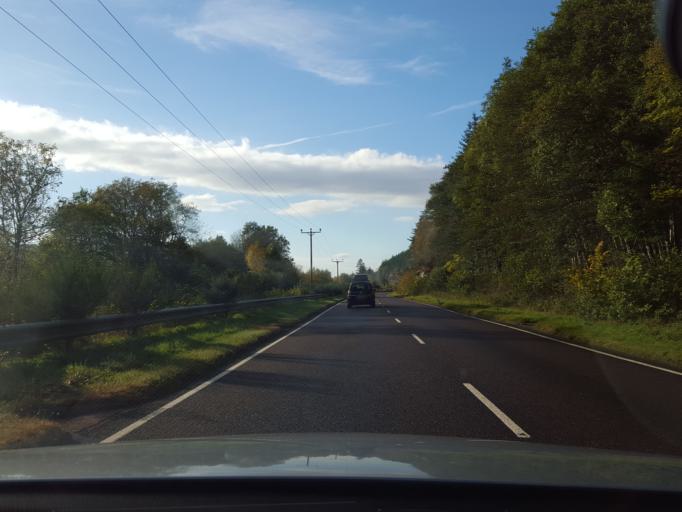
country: GB
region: Scotland
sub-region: Highland
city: Beauly
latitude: 57.2315
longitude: -4.5642
